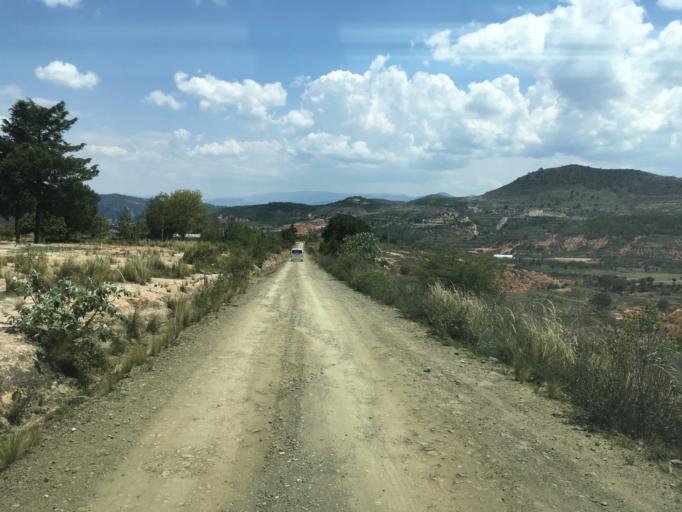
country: MX
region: Oaxaca
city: San Andres Sinaxtla
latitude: 17.6014
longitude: -97.3072
